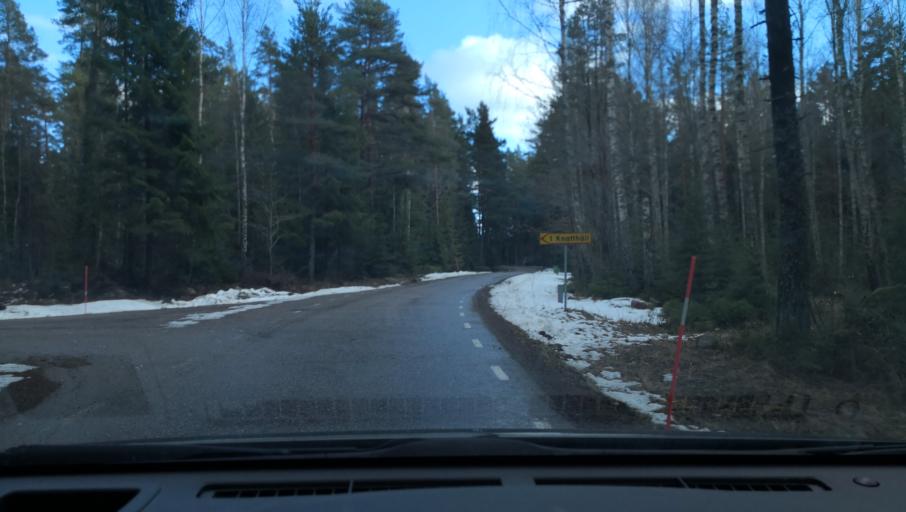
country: SE
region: Vaestmanland
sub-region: Arboga Kommun
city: Arboga
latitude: 59.3337
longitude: 15.7254
